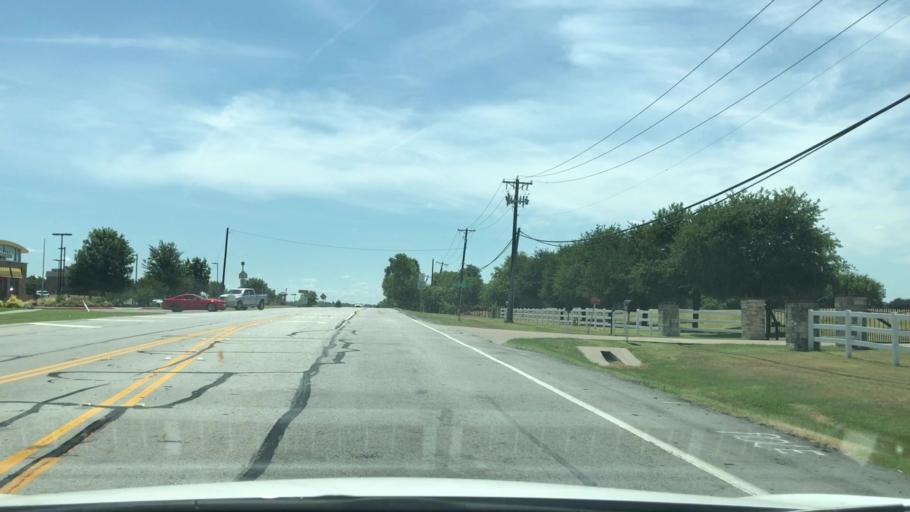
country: US
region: Texas
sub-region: Rockwall County
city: Rockwall
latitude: 32.9646
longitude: -96.4648
